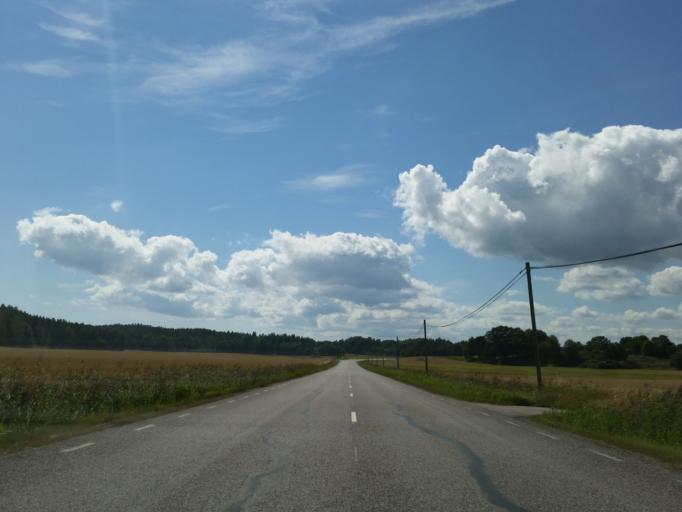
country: SE
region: Soedermanland
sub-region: Trosa Kommun
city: Vagnharad
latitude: 58.9899
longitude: 17.6413
